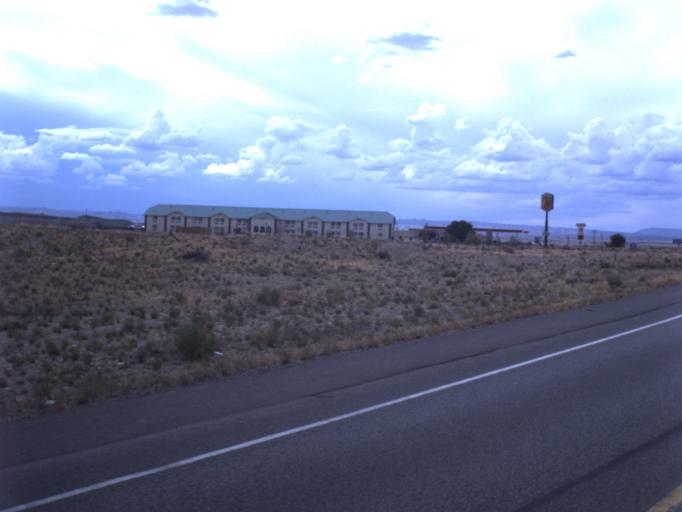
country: US
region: Utah
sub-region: Carbon County
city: East Carbon City
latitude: 38.9896
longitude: -110.1286
